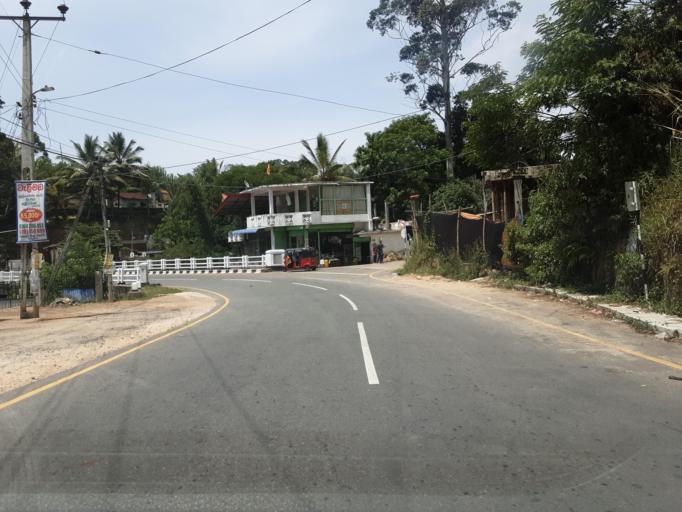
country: LK
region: Uva
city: Badulla
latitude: 6.9619
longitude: 80.9357
